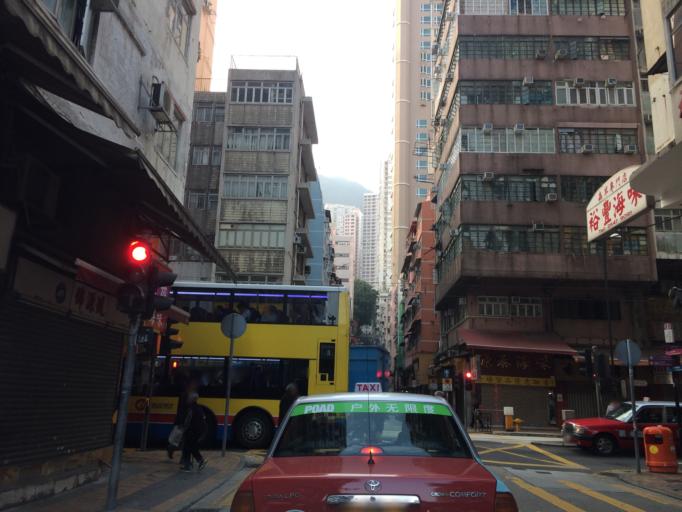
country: HK
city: Hong Kong
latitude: 22.2883
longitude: 114.1439
